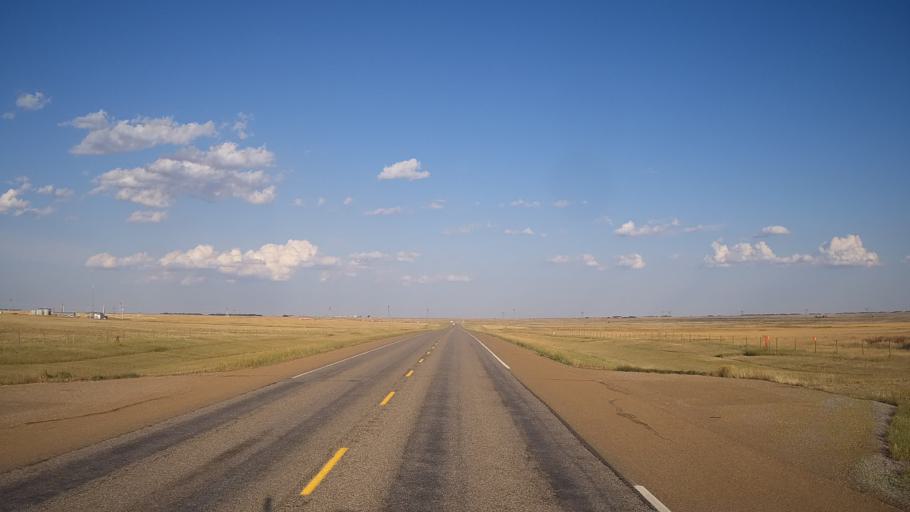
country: CA
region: Alberta
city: Hanna
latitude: 51.6229
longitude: -111.8717
